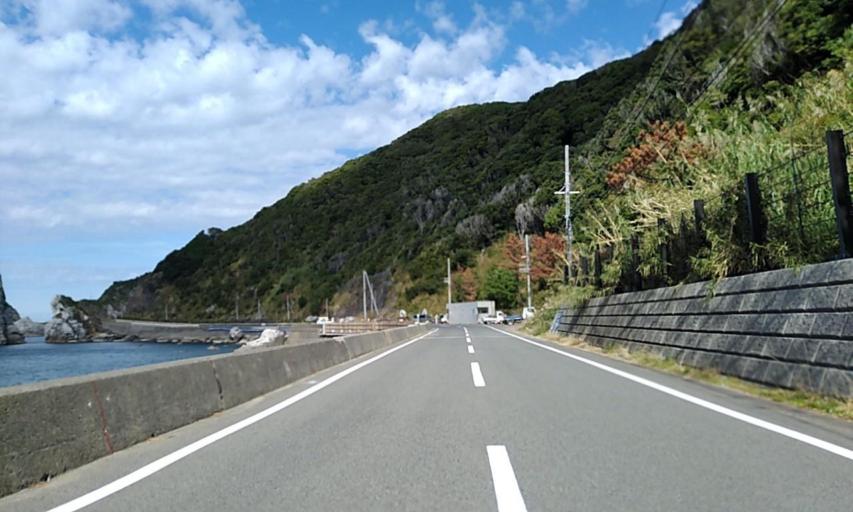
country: JP
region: Wakayama
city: Gobo
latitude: 33.9710
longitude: 135.0795
